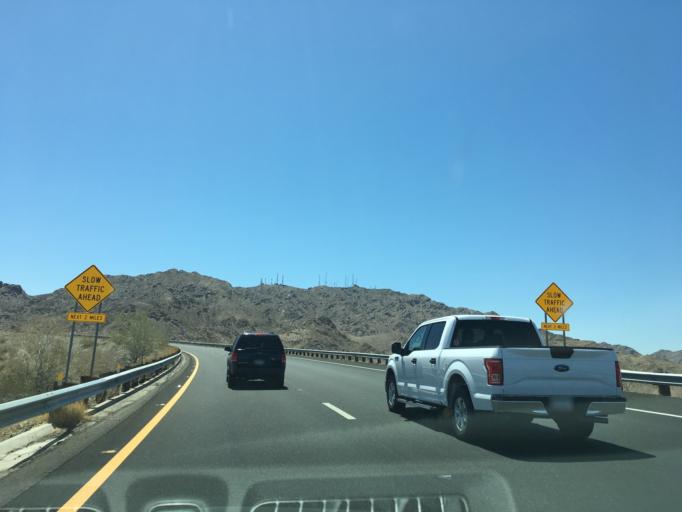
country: US
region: Arizona
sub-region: Yuma County
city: Fortuna Foothills
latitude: 32.6735
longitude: -114.3091
